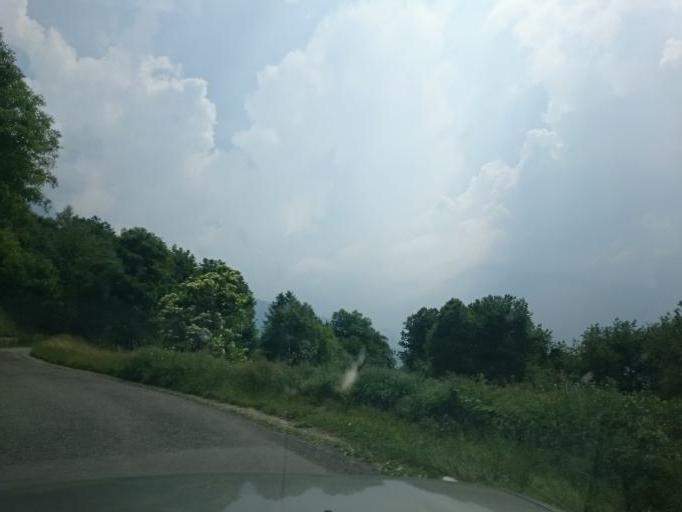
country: IT
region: Lombardy
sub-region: Provincia di Brescia
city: Paspardo
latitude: 46.0341
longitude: 10.3704
